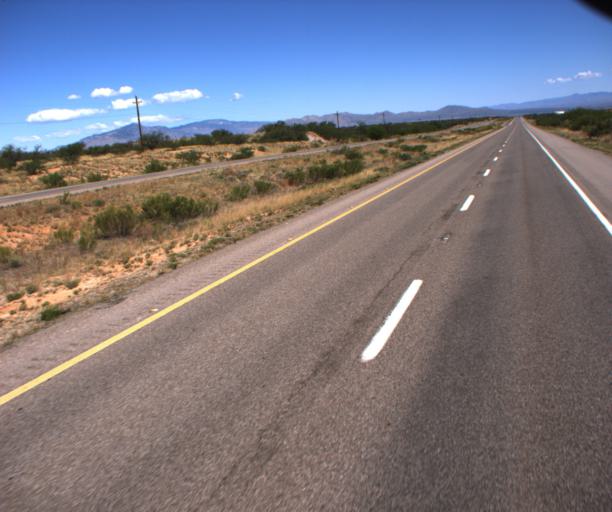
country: US
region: Arizona
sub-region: Cochise County
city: Whetstone
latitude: 31.8966
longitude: -110.3410
